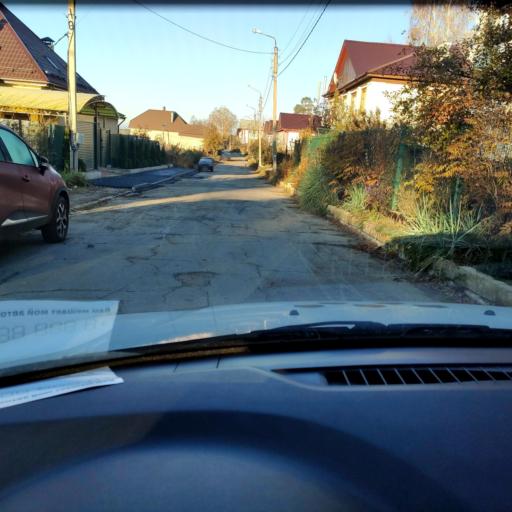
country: RU
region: Samara
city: Tol'yatti
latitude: 53.4744
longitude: 49.3730
